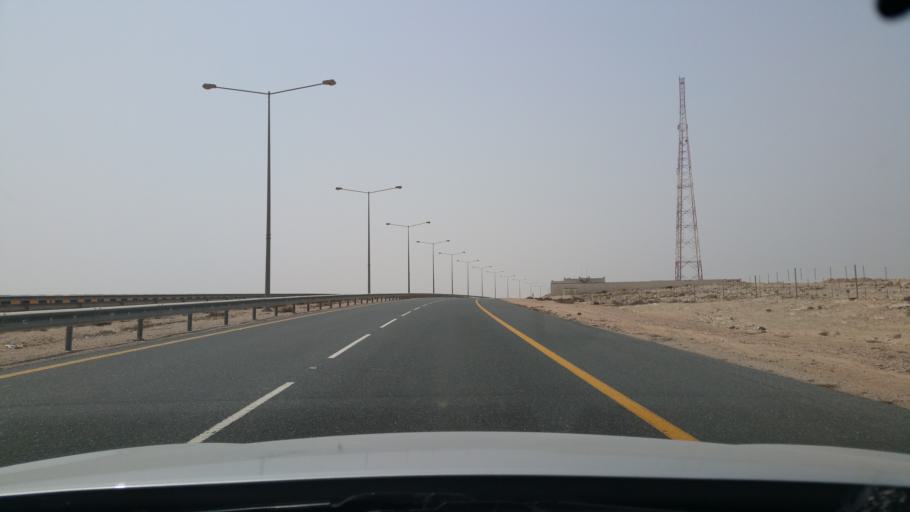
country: QA
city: Umm Bab
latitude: 25.3141
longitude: 50.7916
